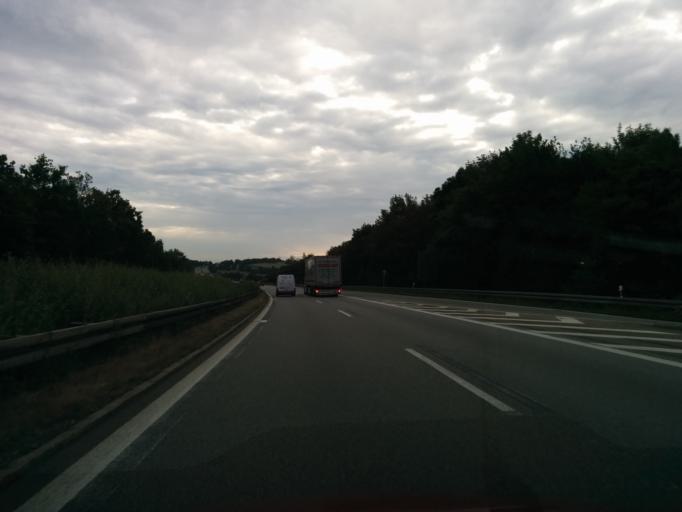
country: DE
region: Bavaria
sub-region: Upper Palatinate
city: Sinzing
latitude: 48.9950
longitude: 12.0278
